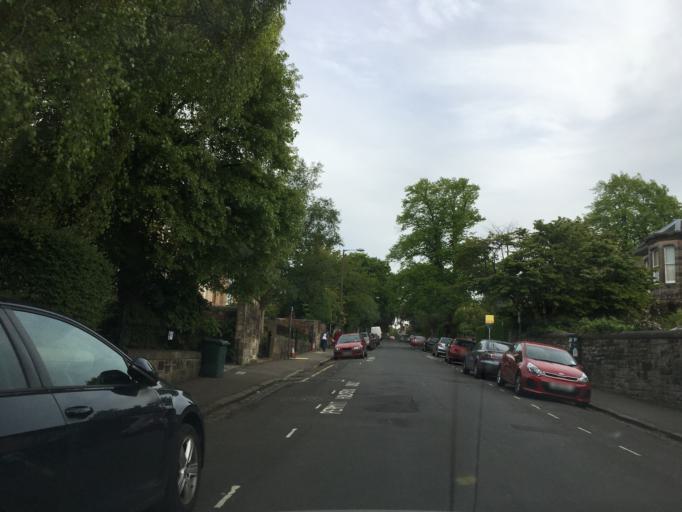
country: GB
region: Scotland
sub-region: Edinburgh
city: Edinburgh
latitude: 55.9368
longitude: -3.2152
